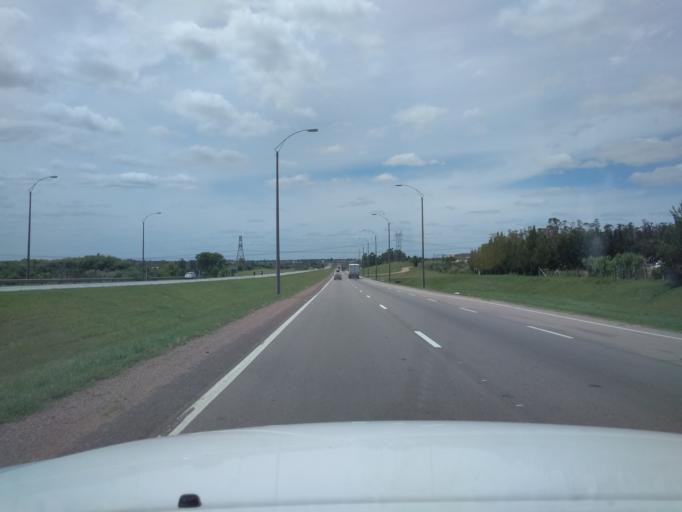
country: UY
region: Canelones
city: La Paz
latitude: -34.7660
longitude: -56.2652
